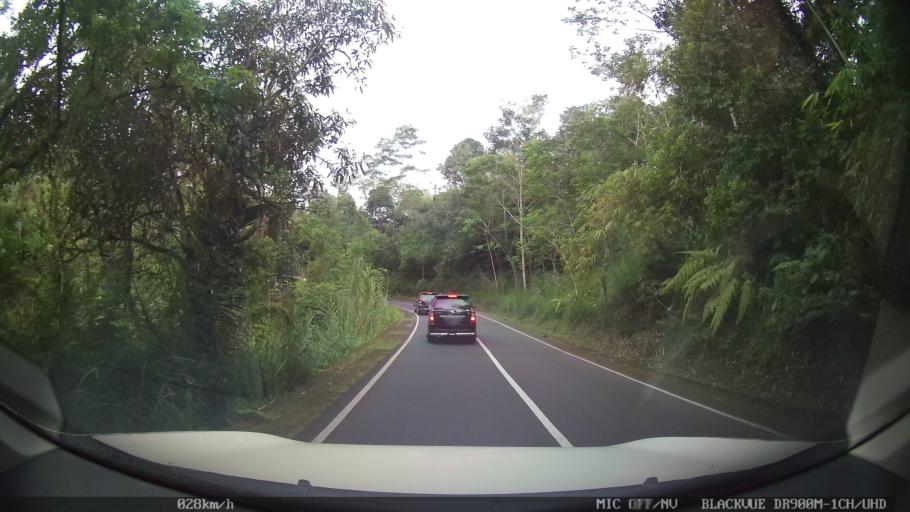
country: ID
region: Bali
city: Banjar Bias
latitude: -8.3719
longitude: 115.4192
